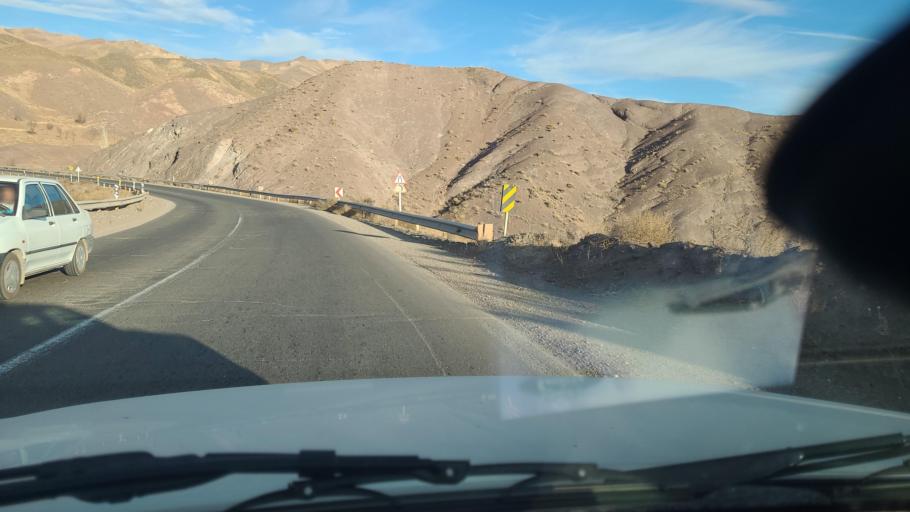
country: IR
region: Razavi Khorasan
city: Sabzevar
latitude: 36.4184
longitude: 57.5643
